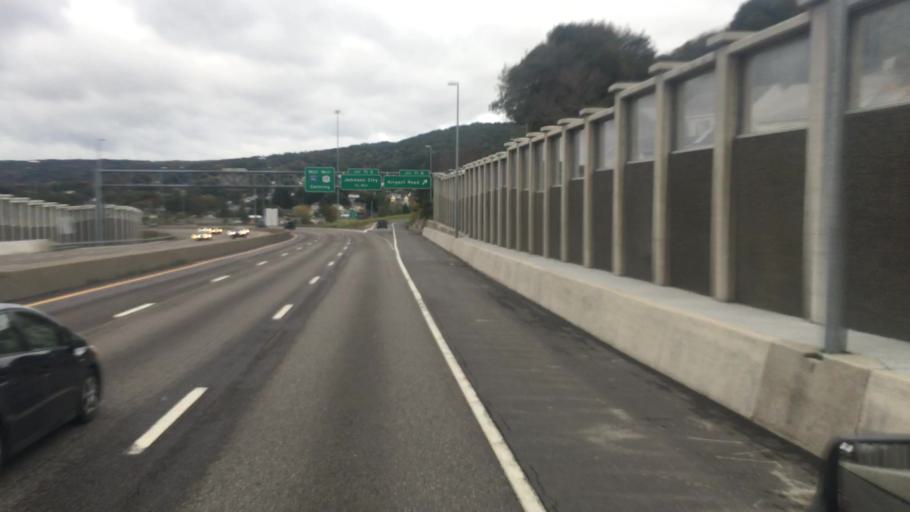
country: US
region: New York
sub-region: Broome County
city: Johnson City
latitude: 42.1185
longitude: -75.9421
